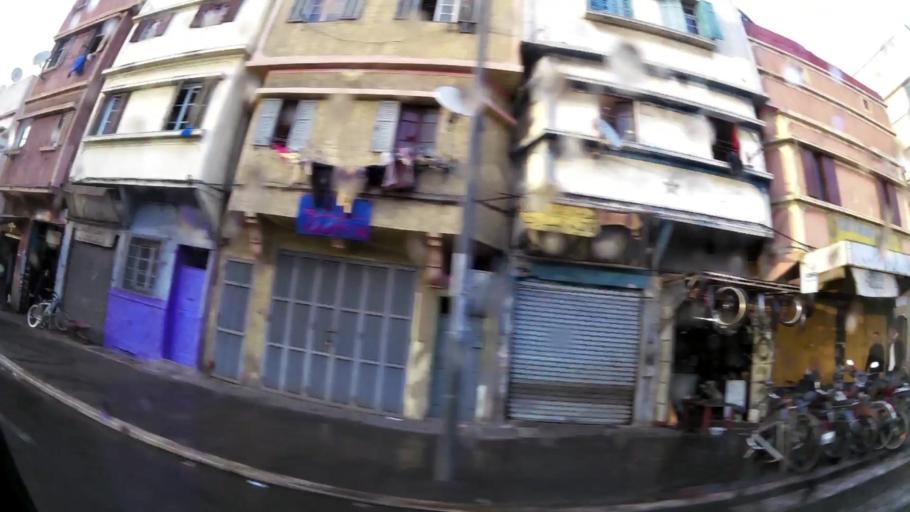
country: MA
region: Grand Casablanca
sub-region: Casablanca
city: Casablanca
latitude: 33.5817
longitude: -7.5658
